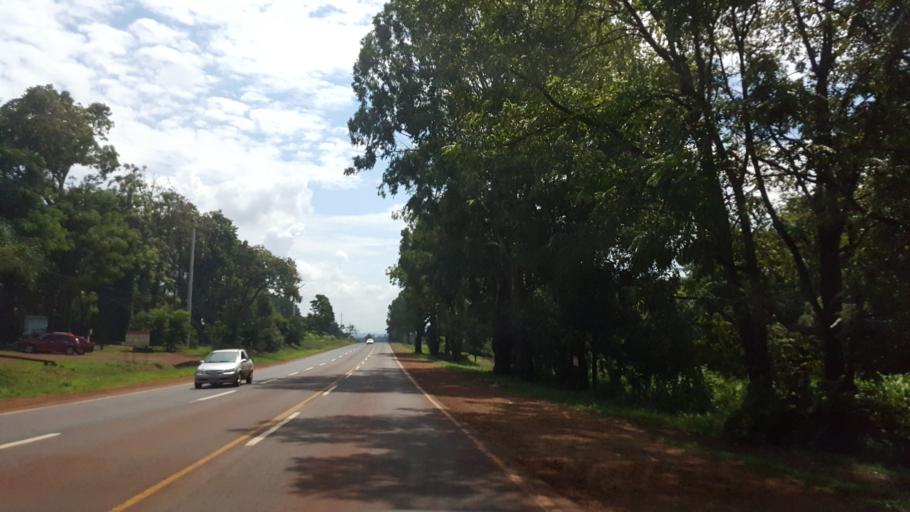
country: AR
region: Misiones
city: Puerto Rico
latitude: -26.8409
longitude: -55.0398
